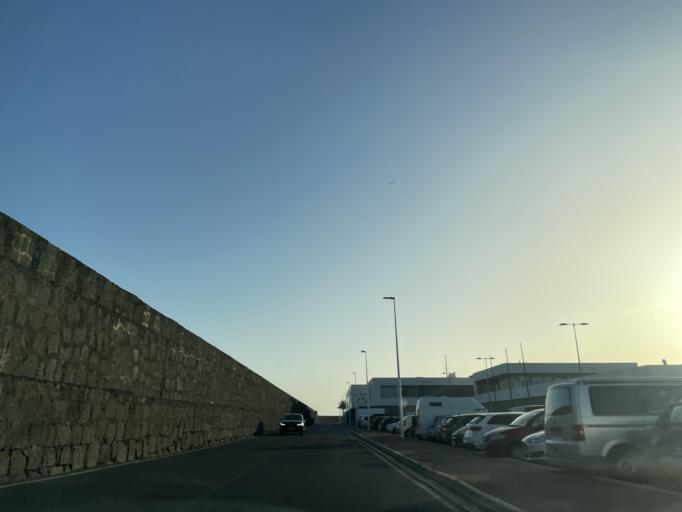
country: ES
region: Canary Islands
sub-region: Provincia de Las Palmas
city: Arrecife
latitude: 28.9623
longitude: -13.5385
